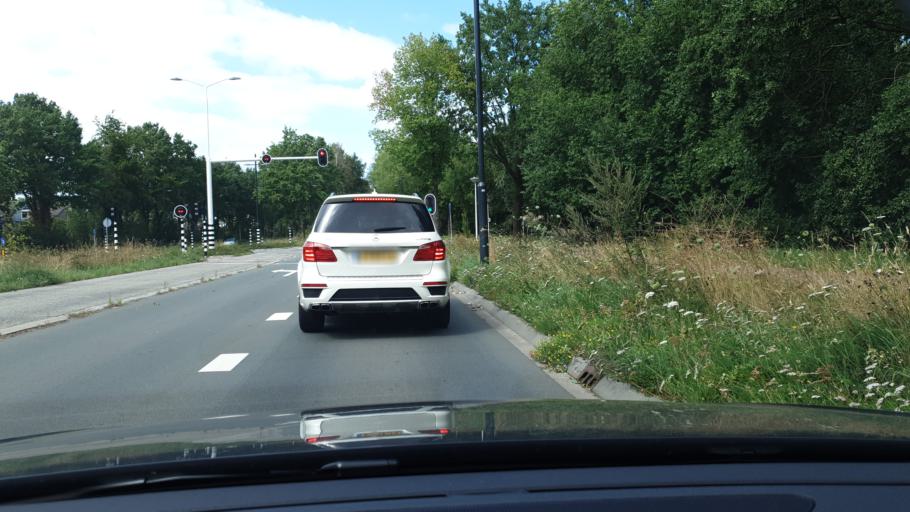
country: NL
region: North Brabant
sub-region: Gemeente Son en Breugel
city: Son
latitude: 51.4866
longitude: 5.4532
